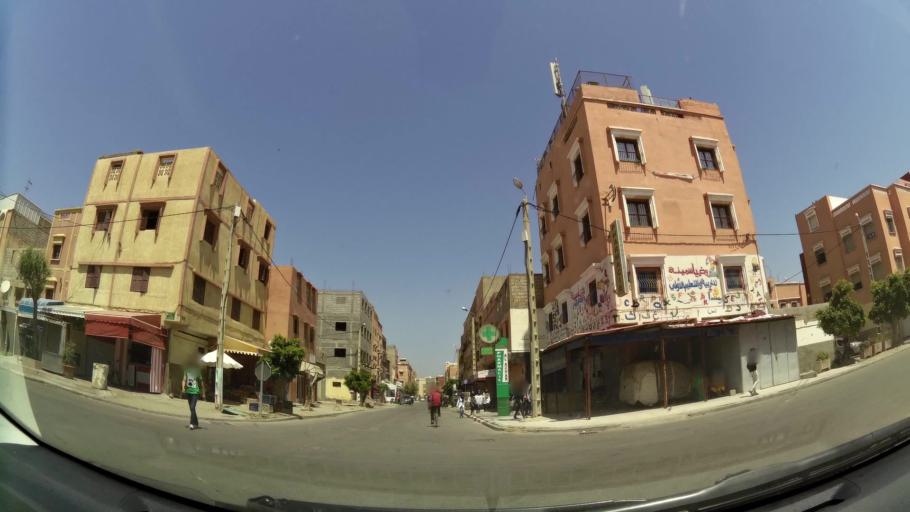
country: MA
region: Souss-Massa-Draa
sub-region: Inezgane-Ait Mellou
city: Inezgane
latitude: 30.3482
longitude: -9.4903
